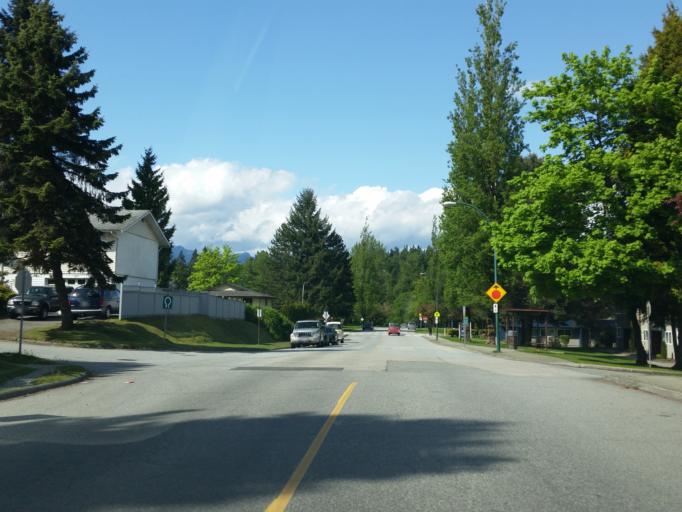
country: CA
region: British Columbia
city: Port Moody
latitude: 49.2776
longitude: -122.8755
